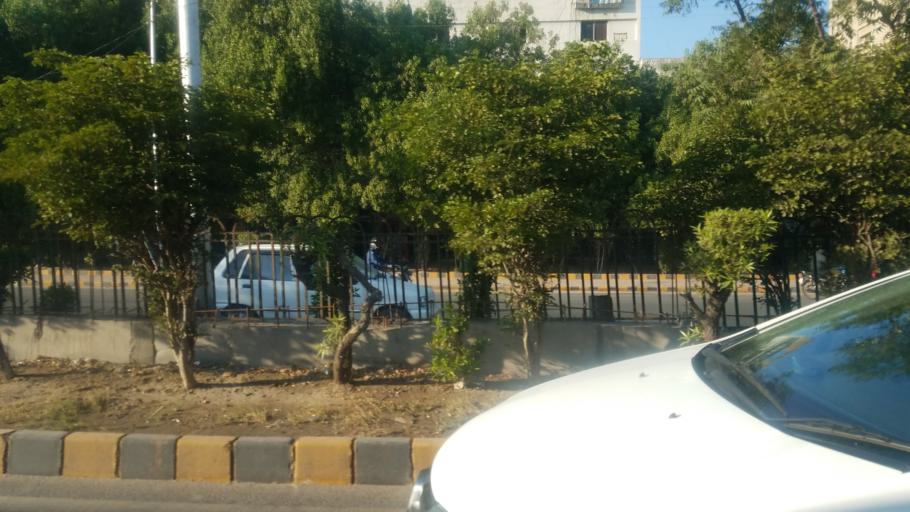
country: PK
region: Sindh
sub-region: Karachi District
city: Karachi
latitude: 24.8597
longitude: 67.0602
